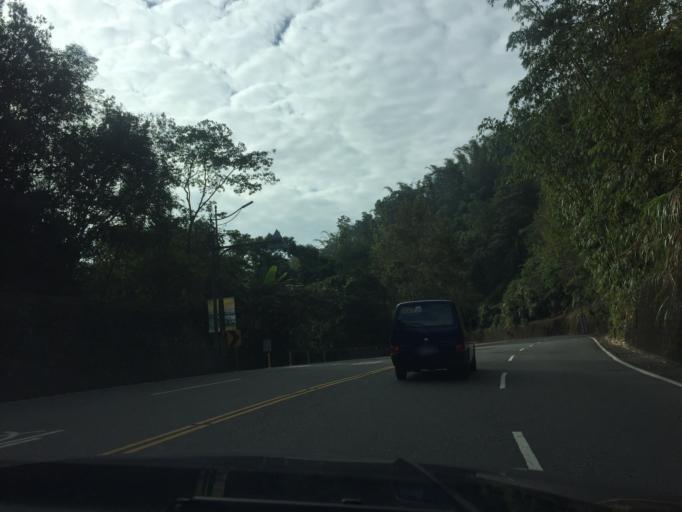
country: TW
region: Taiwan
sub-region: Nantou
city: Puli
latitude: 23.8590
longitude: 120.9007
